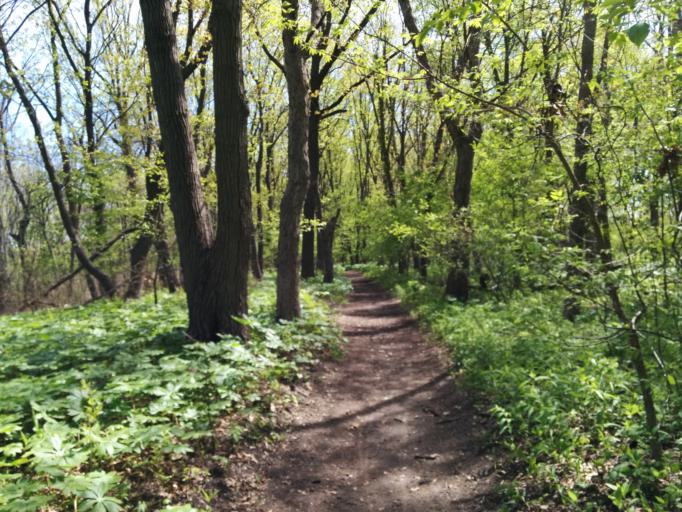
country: US
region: Indiana
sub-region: Lake County
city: Whiting
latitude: 41.6838
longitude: -87.5295
